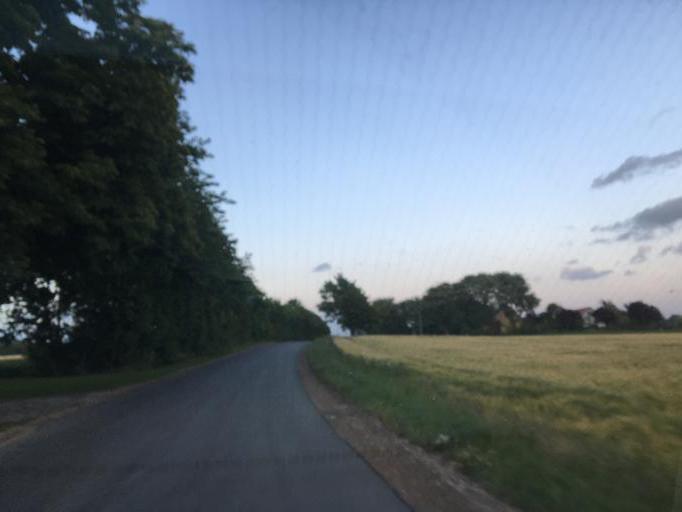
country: DK
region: Zealand
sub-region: Solrod Kommune
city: Havdrup
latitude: 55.5219
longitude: 12.1084
